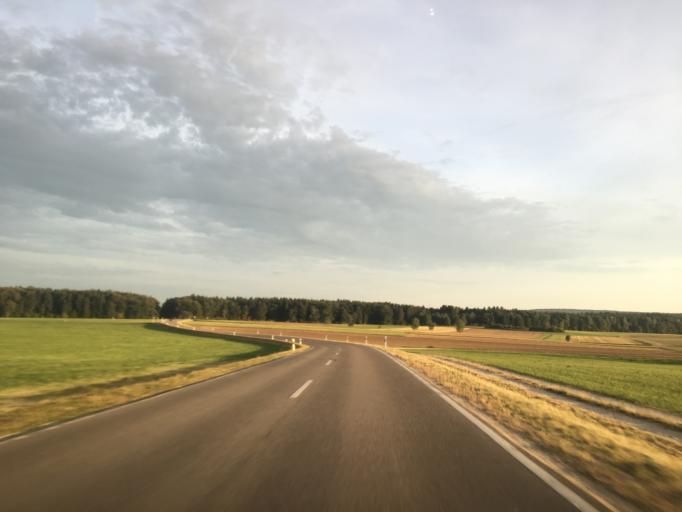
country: DE
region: Baden-Wuerttemberg
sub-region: Tuebingen Region
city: Hayingen
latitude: 48.3097
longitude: 9.4455
